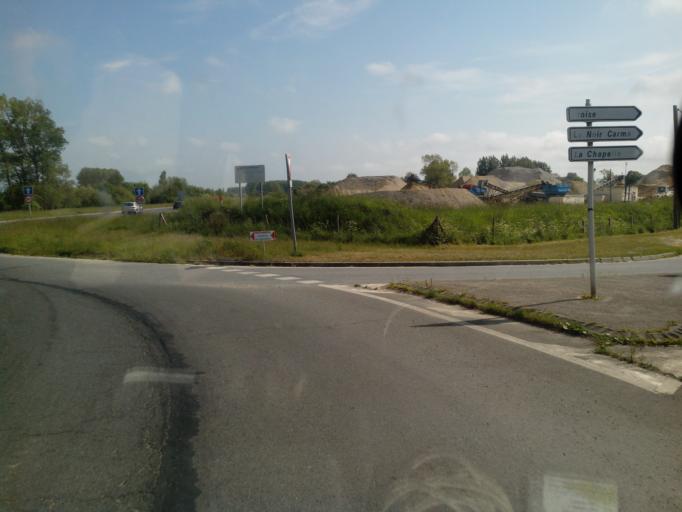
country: FR
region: Picardie
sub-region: Departement de la Somme
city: Quend
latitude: 50.2947
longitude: 1.6505
